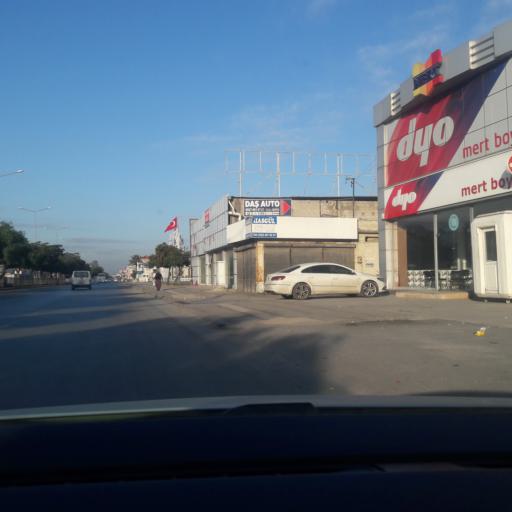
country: TR
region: Adana
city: Seyhan
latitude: 36.9955
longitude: 35.2732
